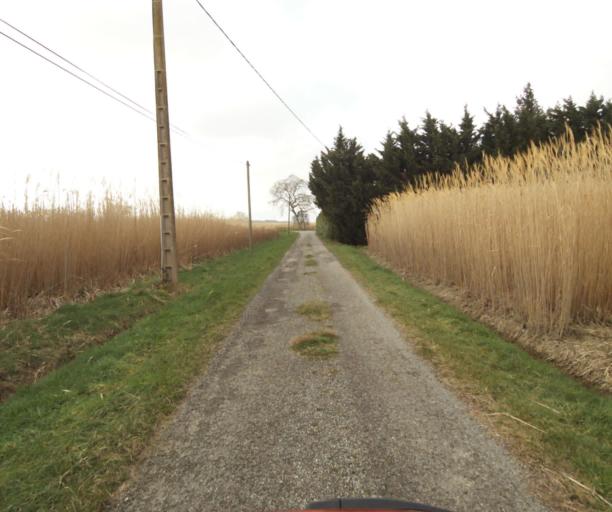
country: FR
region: Midi-Pyrenees
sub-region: Departement de l'Ariege
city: Mazeres
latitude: 43.1942
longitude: 1.6704
